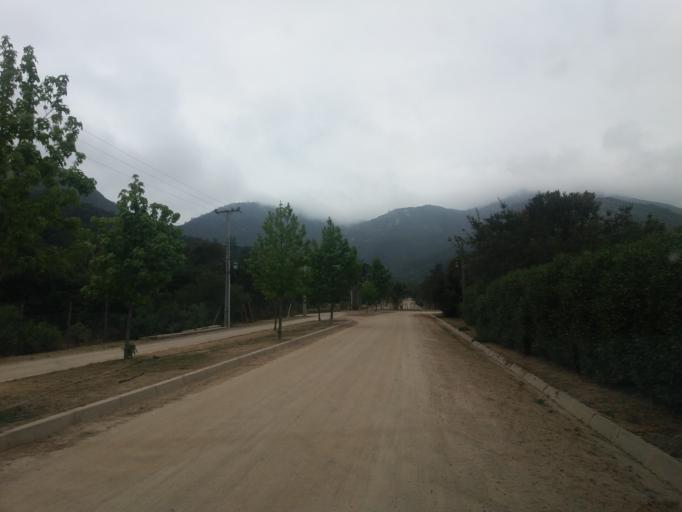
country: CL
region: Valparaiso
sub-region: Provincia de Marga Marga
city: Limache
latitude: -33.0266
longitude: -71.1328
